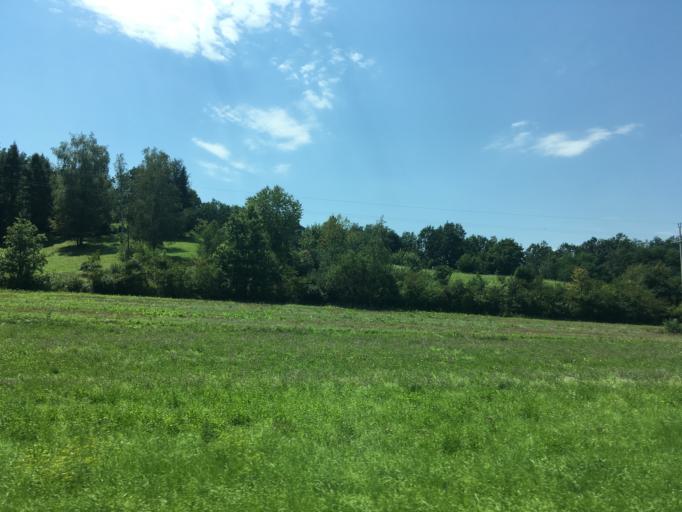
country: SI
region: Metlika
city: Metlika
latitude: 45.6101
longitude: 15.3289
